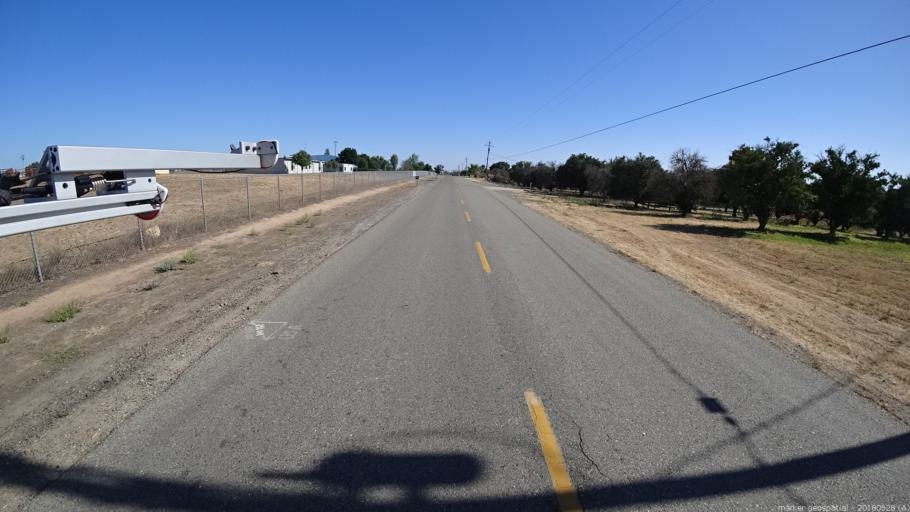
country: US
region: California
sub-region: Madera County
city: Bonadelle Ranchos-Madera Ranchos
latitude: 36.9855
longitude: -119.8794
